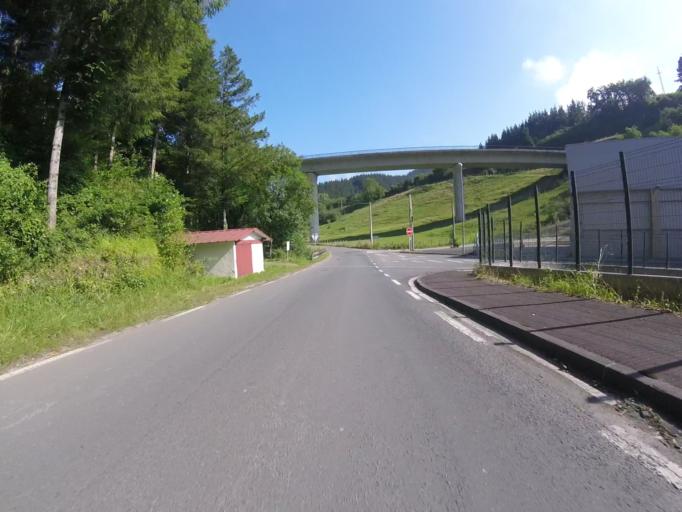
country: ES
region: Basque Country
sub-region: Provincia de Guipuzcoa
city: Ormaiztegui
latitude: 43.0532
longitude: -2.2341
